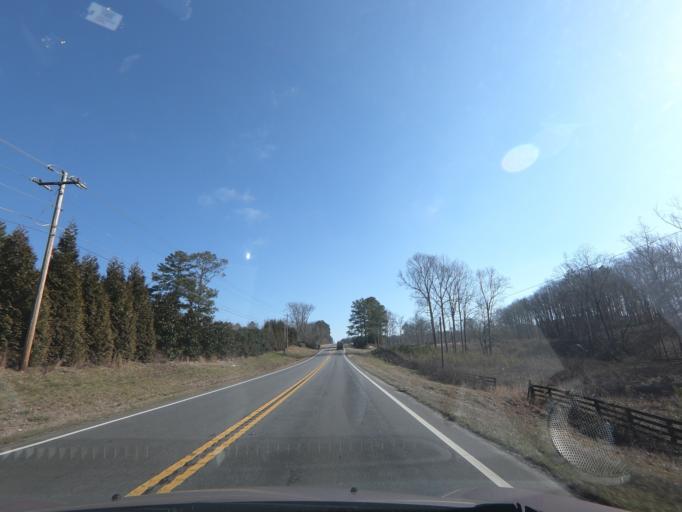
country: US
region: Georgia
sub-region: Forsyth County
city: Cumming
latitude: 34.2990
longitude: -84.2342
